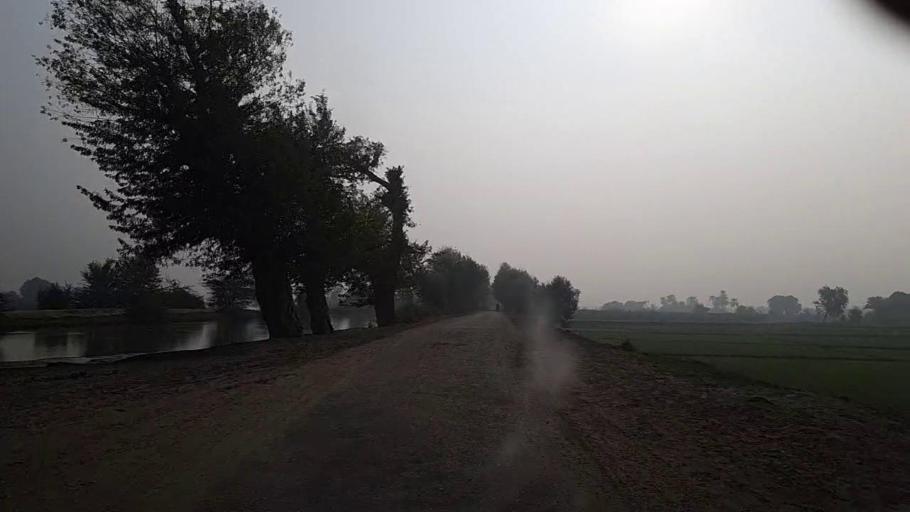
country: PK
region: Sindh
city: Bozdar
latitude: 27.1477
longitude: 68.6600
